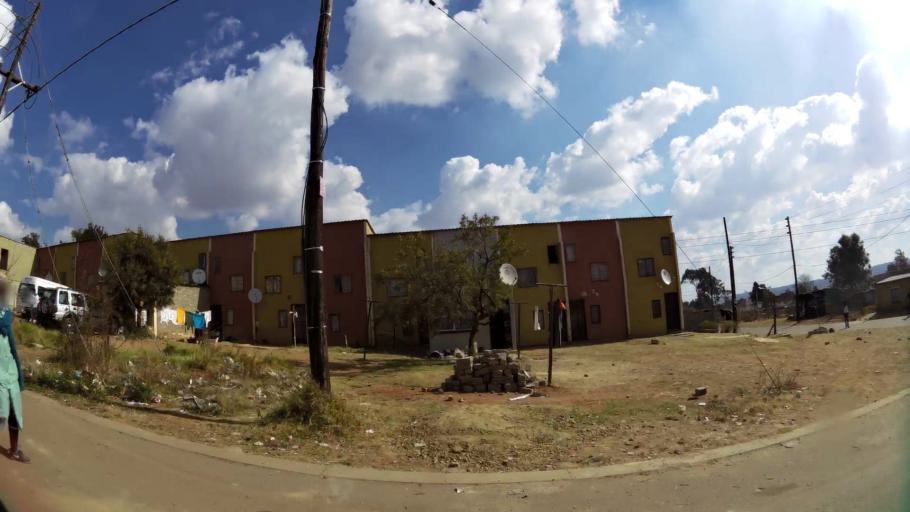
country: ZA
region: Gauteng
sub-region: City of Johannesburg Metropolitan Municipality
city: Roodepoort
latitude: -26.1840
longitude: 27.8406
